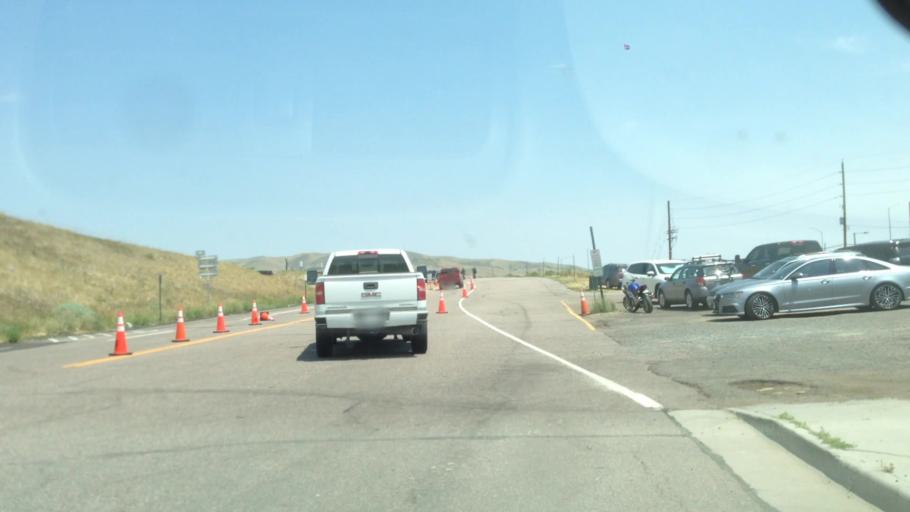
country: US
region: Colorado
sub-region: Jefferson County
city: Indian Hills
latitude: 39.6532
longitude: -105.1834
